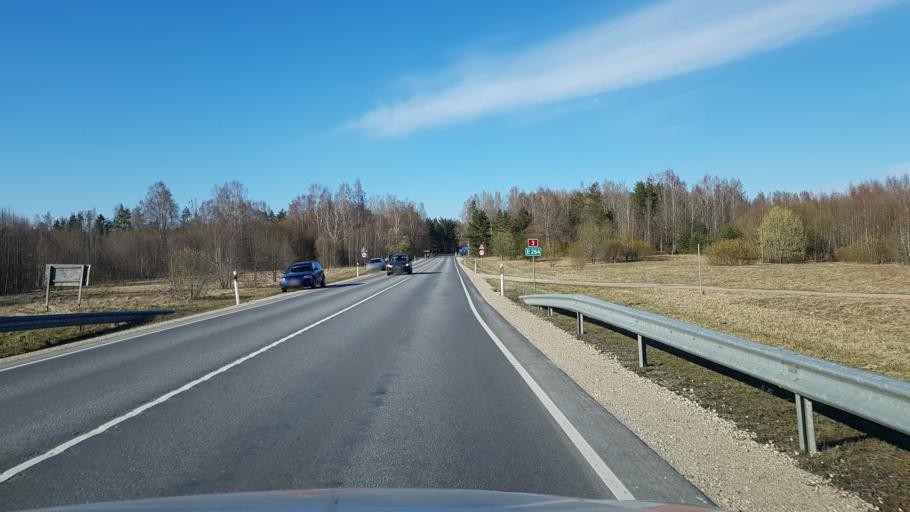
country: EE
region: Jogevamaa
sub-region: Mustvee linn
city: Mustvee
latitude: 58.9870
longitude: 27.1725
